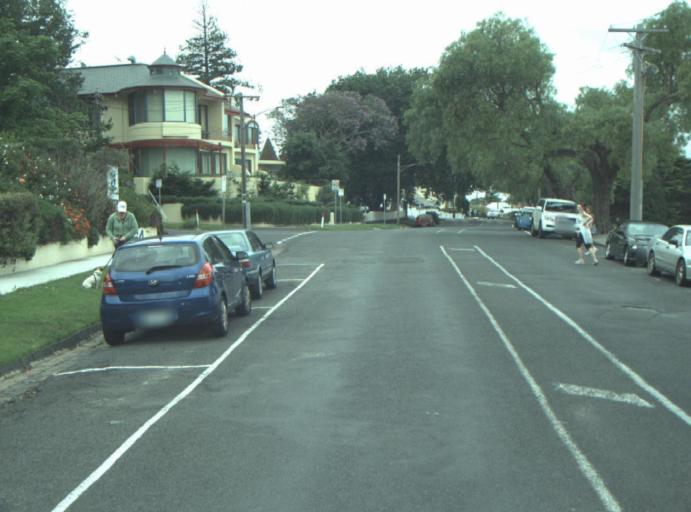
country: AU
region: Victoria
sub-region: Greater Geelong
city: East Geelong
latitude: -38.1480
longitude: 144.3736
